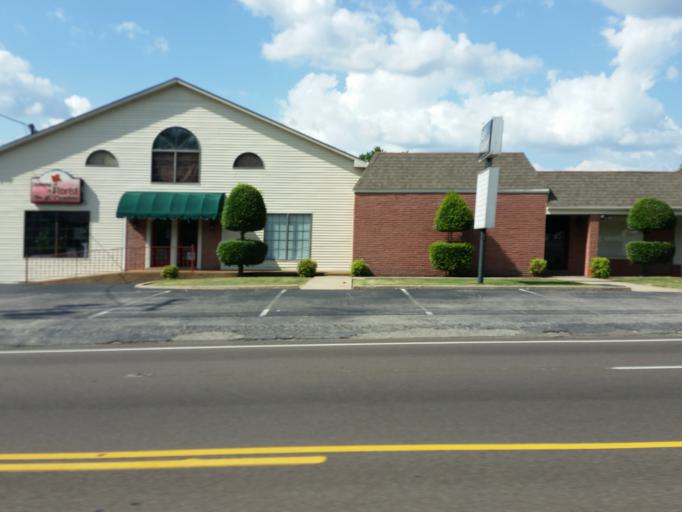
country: US
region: Tennessee
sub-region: Henderson County
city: Lexington
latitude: 35.6550
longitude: -88.4019
